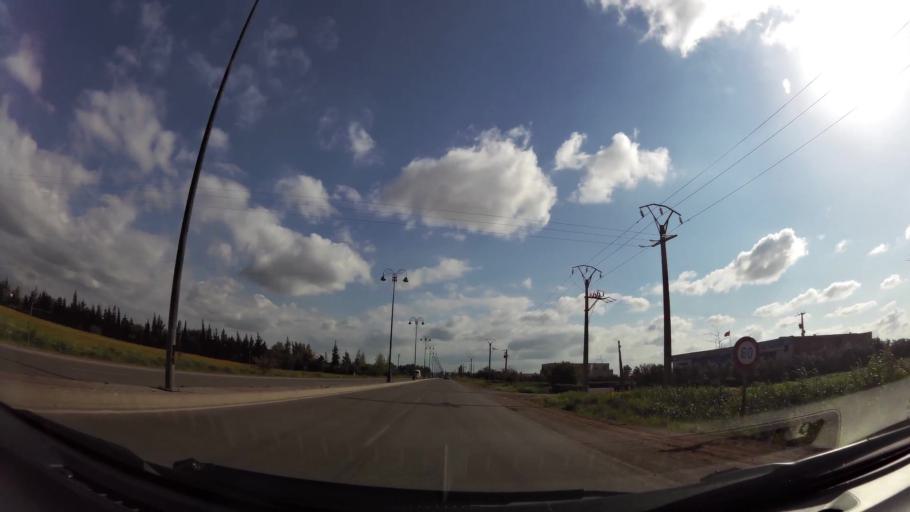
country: MA
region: Chaouia-Ouardigha
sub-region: Settat Province
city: Berrechid
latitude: 33.2945
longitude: -7.5747
